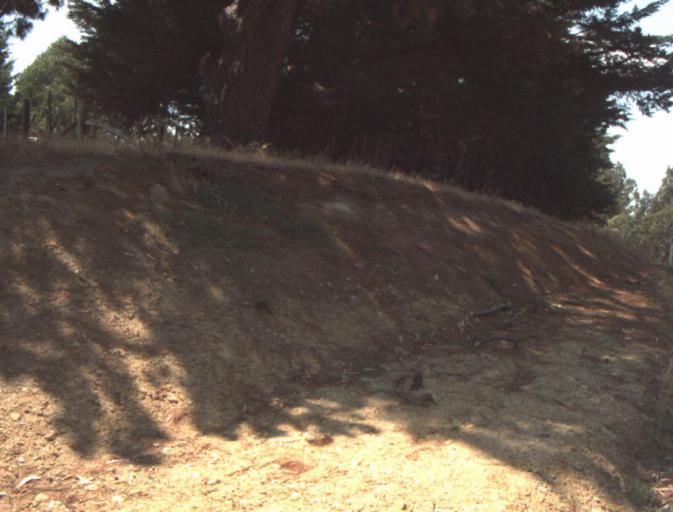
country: AU
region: Tasmania
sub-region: Launceston
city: Newstead
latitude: -41.4711
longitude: 147.1899
